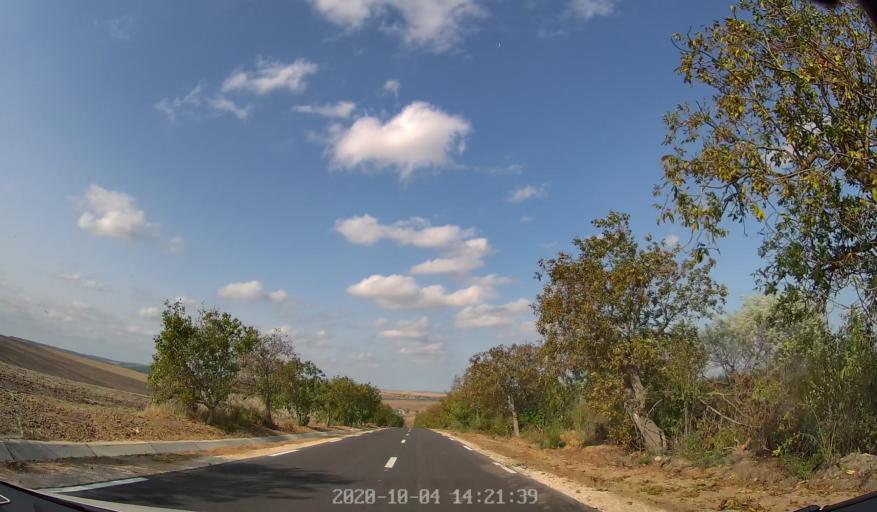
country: MD
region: Rezina
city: Saharna
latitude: 47.5875
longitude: 28.9544
